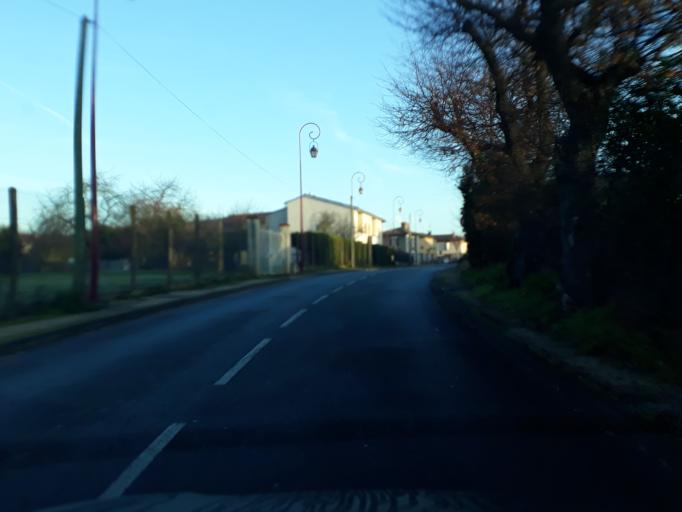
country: FR
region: Midi-Pyrenees
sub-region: Departement de la Haute-Garonne
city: Longages
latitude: 43.3545
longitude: 1.2361
